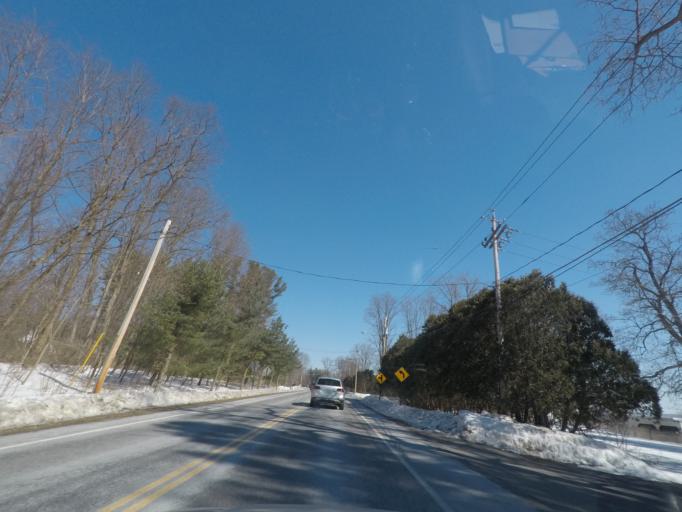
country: US
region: New York
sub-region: Saratoga County
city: Saratoga Springs
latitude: 43.0531
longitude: -73.7307
